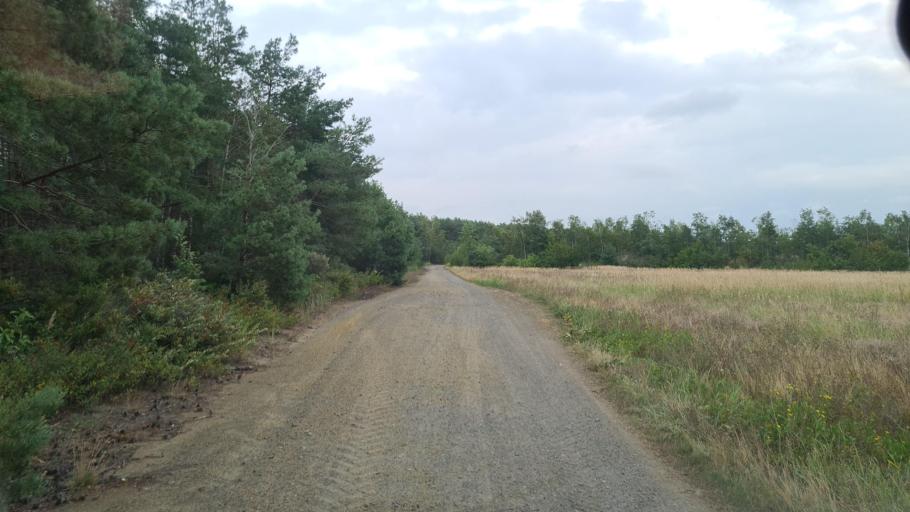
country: DE
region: Brandenburg
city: Finsterwalde
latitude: 51.5727
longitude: 13.7342
